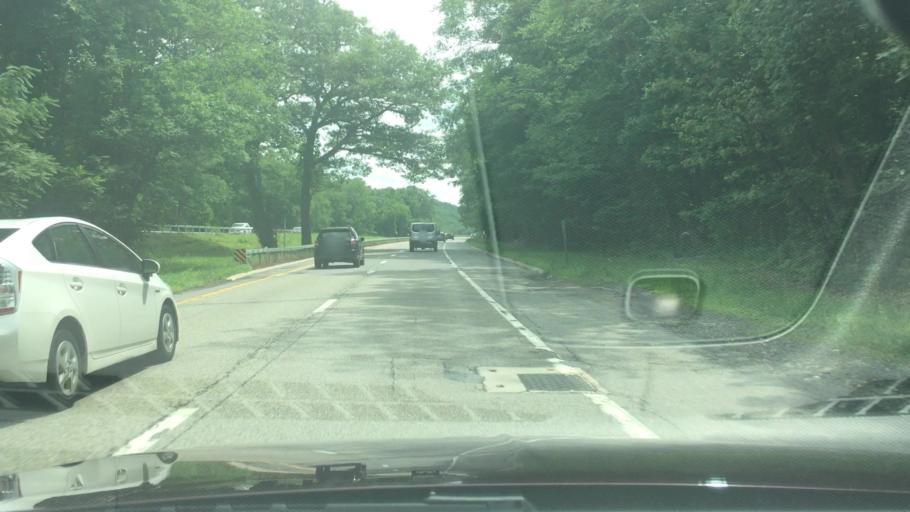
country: US
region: New York
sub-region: Putnam County
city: Mahopac
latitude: 41.4455
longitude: -73.8161
